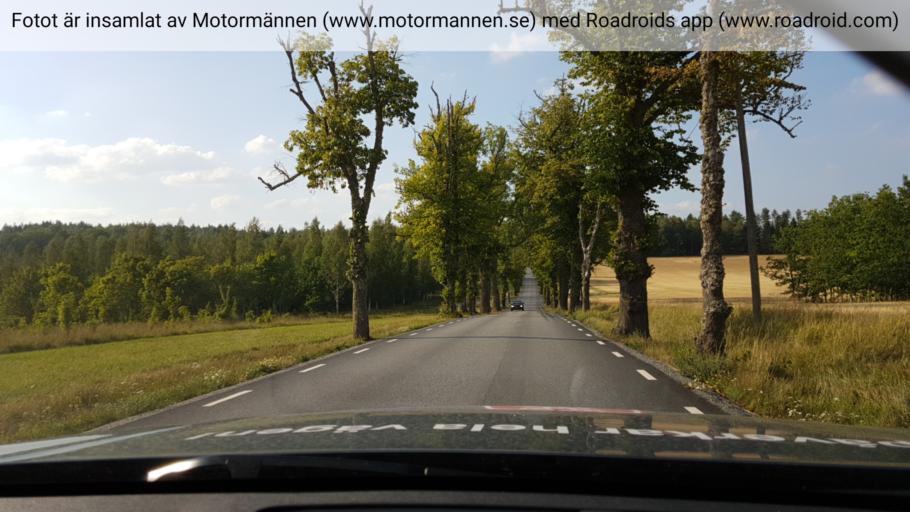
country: SE
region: Soedermanland
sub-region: Strangnas Kommun
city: Mariefred
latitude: 59.1424
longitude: 17.2102
